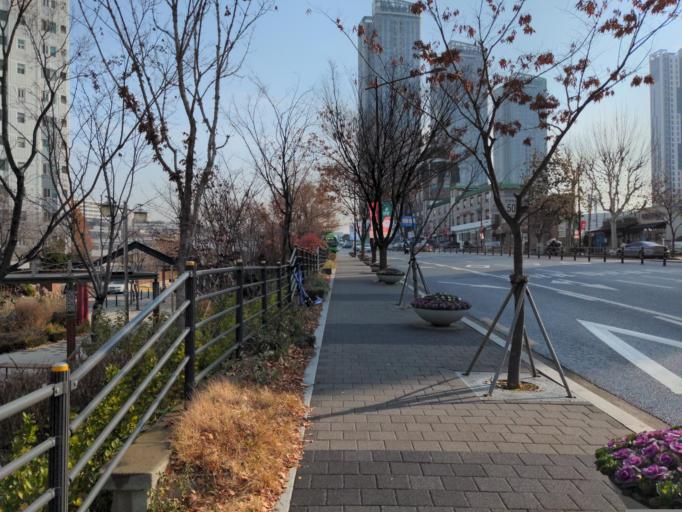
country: KR
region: Seoul
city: Seoul
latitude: 37.5591
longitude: 127.0374
